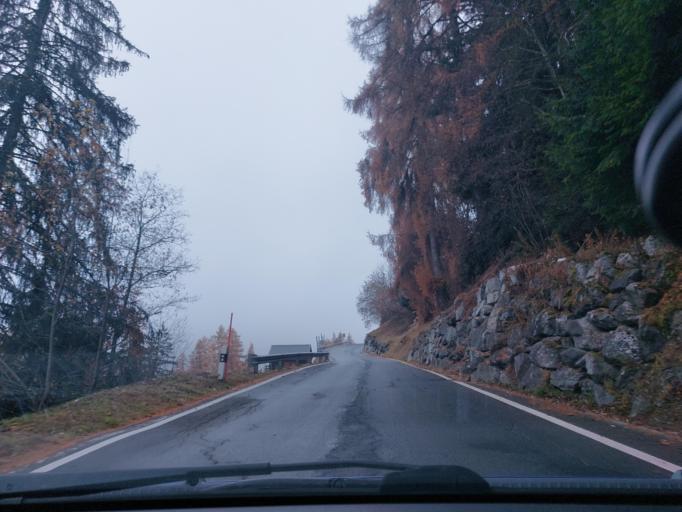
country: CH
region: Valais
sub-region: Conthey District
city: Basse-Nendaz
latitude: 46.1687
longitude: 7.3111
